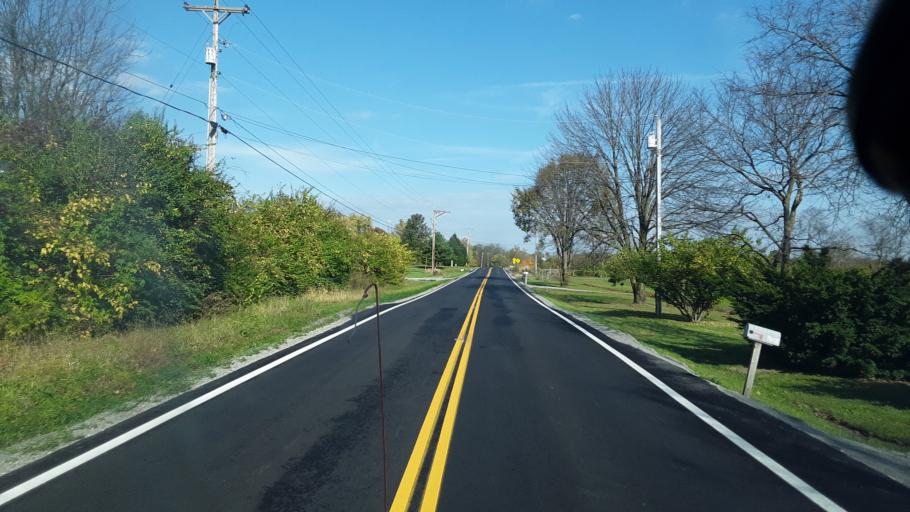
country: US
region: Ohio
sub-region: Highland County
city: Leesburg
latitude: 39.3599
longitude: -83.5892
